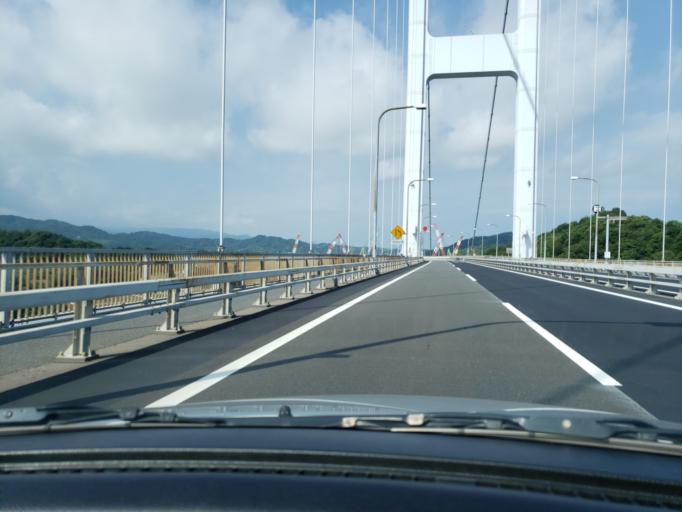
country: JP
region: Hiroshima
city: Takehara
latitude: 34.1138
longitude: 132.9809
